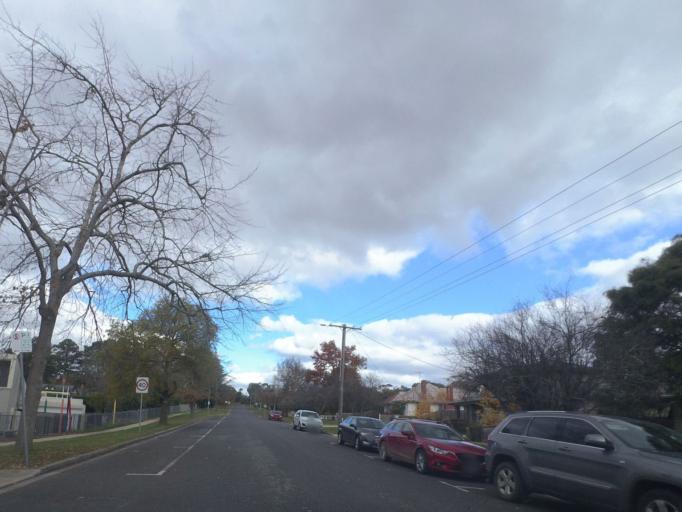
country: AU
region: Victoria
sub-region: Hume
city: Sunbury
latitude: -37.4904
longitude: 144.5876
